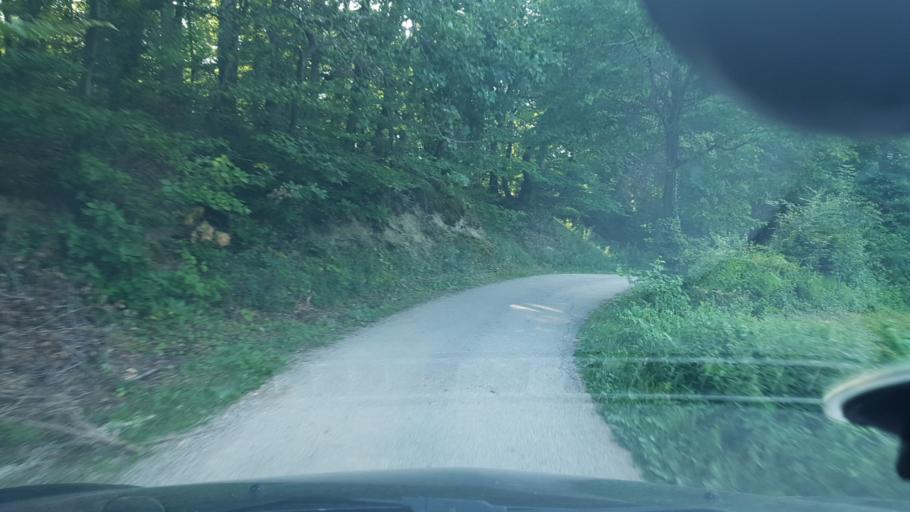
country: HR
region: Krapinsko-Zagorska
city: Radoboj
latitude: 46.1735
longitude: 15.9013
